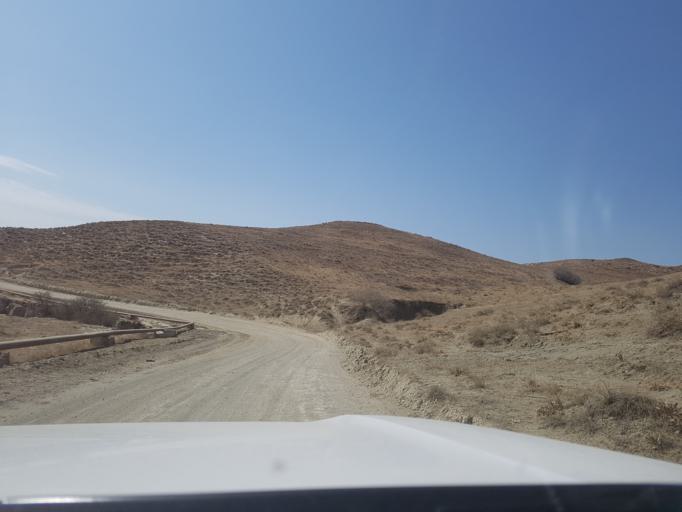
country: TM
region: Ahal
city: Baharly
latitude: 38.2478
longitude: 56.8922
